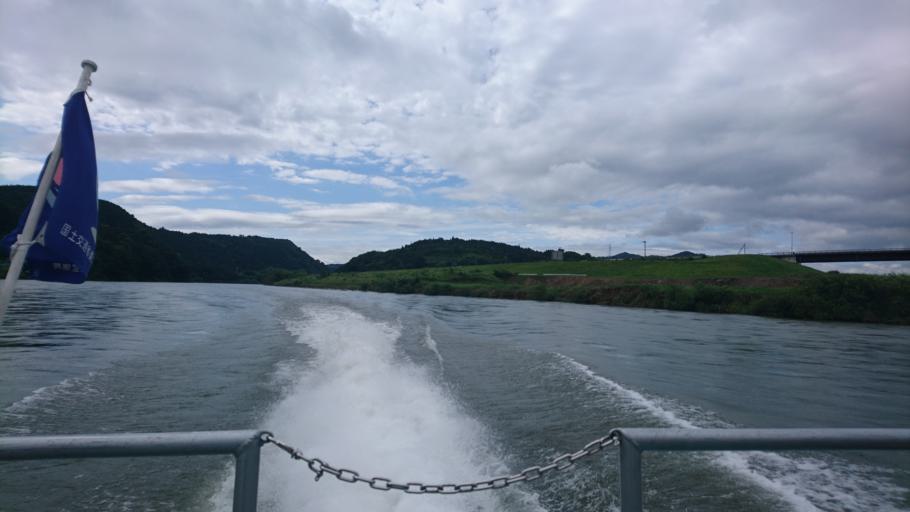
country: JP
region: Iwate
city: Ichinoseki
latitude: 38.9013
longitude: 141.2595
